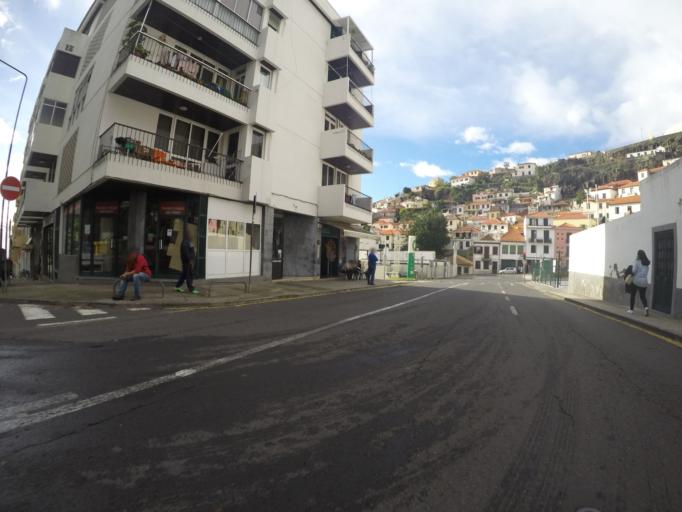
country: PT
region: Madeira
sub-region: Funchal
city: Nossa Senhora do Monte
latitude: 32.6556
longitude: -16.9147
